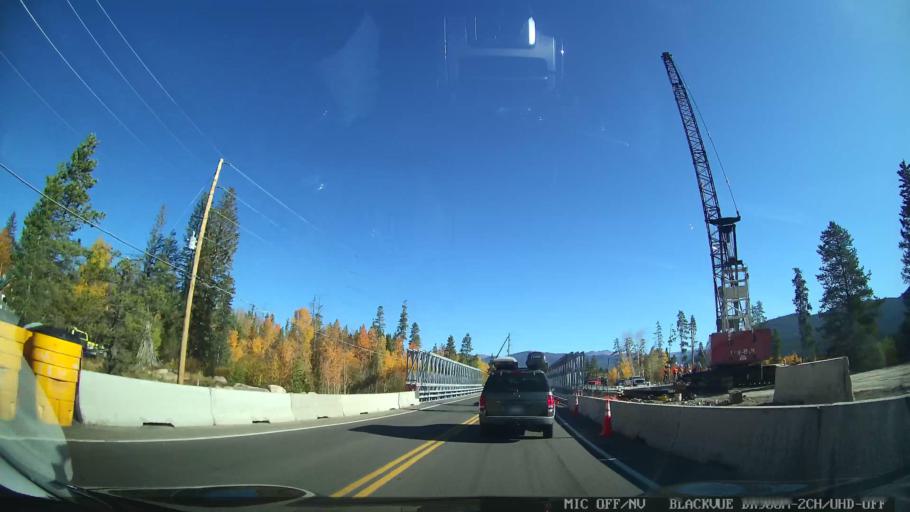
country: US
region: Colorado
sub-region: Grand County
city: Granby
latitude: 40.2192
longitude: -105.8590
